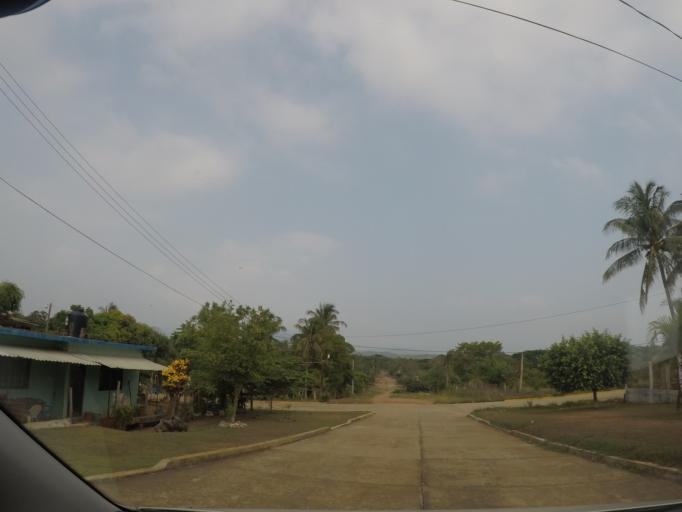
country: MX
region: Oaxaca
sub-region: Santa Maria Petapa
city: Llano Suchiapa
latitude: 16.8691
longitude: -95.0493
